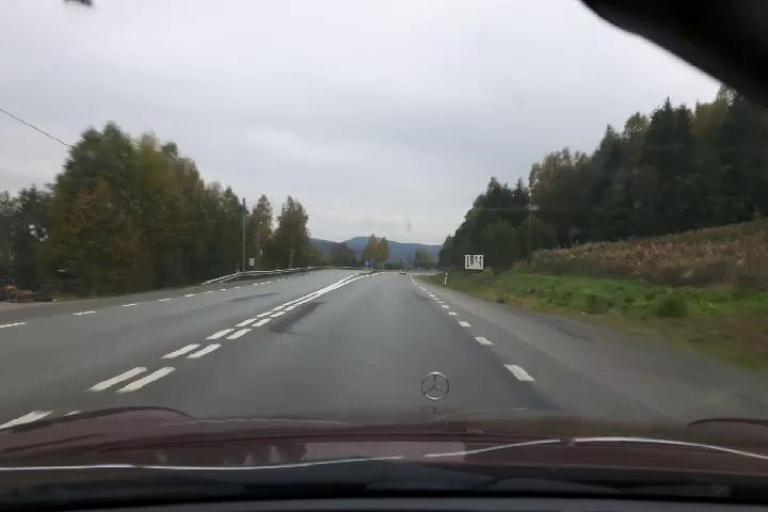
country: SE
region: Vaesternorrland
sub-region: Kramfors Kommun
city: Nordingra
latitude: 63.0081
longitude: 18.2877
